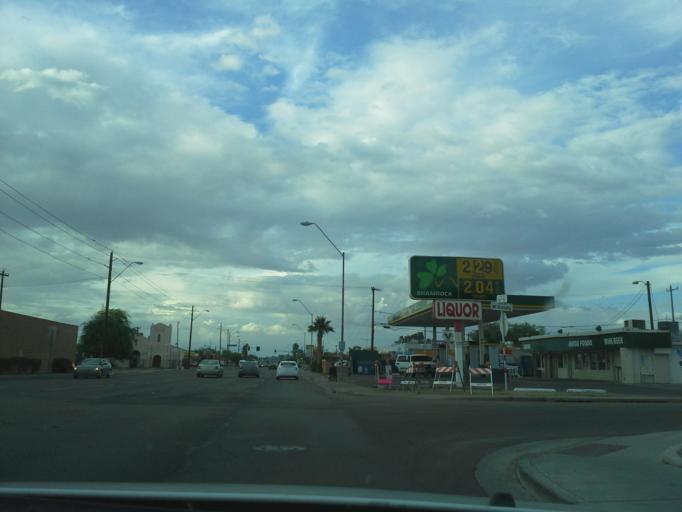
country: US
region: Arizona
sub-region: Maricopa County
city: Phoenix
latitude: 33.4566
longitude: -112.0476
